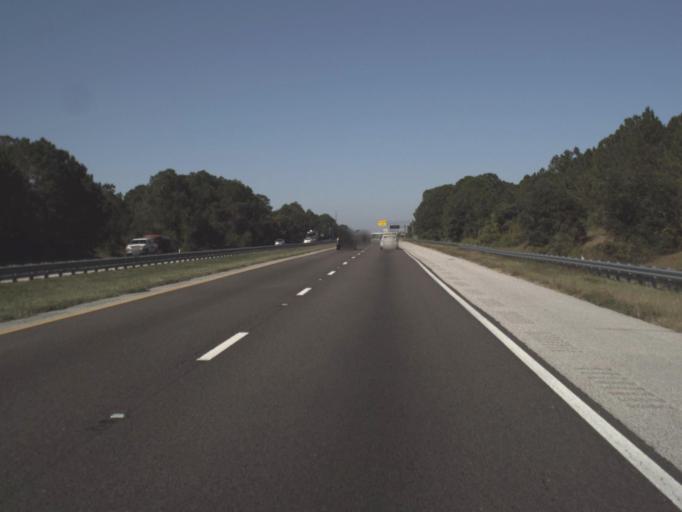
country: US
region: Florida
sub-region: Lake County
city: Howie In The Hills
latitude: 28.6594
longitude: -81.8217
